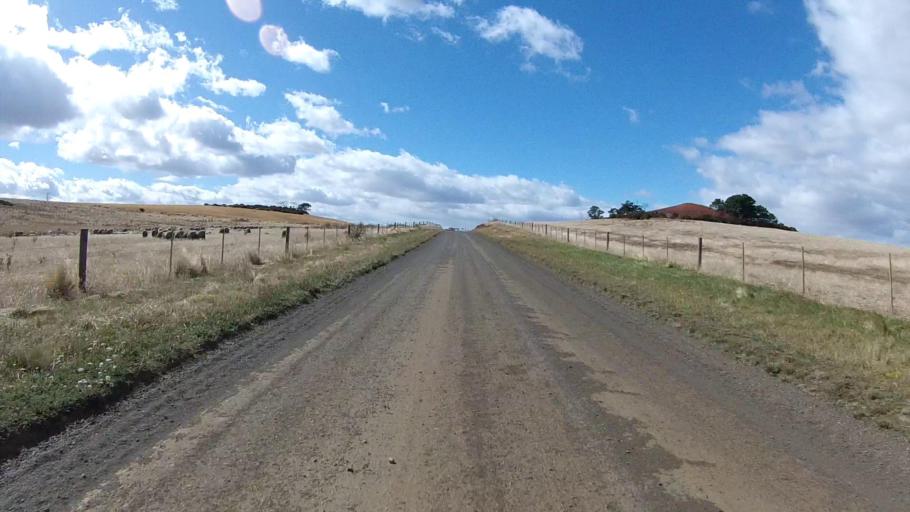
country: AU
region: Tasmania
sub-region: Northern Midlands
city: Evandale
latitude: -41.7151
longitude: 147.4170
